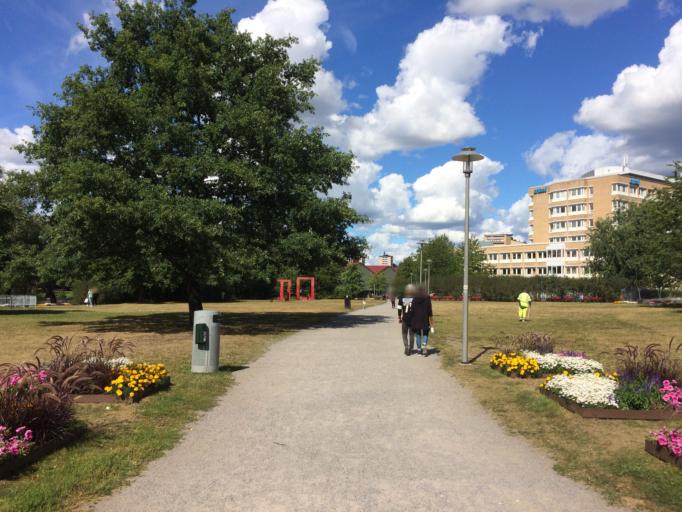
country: SE
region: Stockholm
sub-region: Stockholms Kommun
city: Arsta
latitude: 59.3109
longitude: 18.0217
